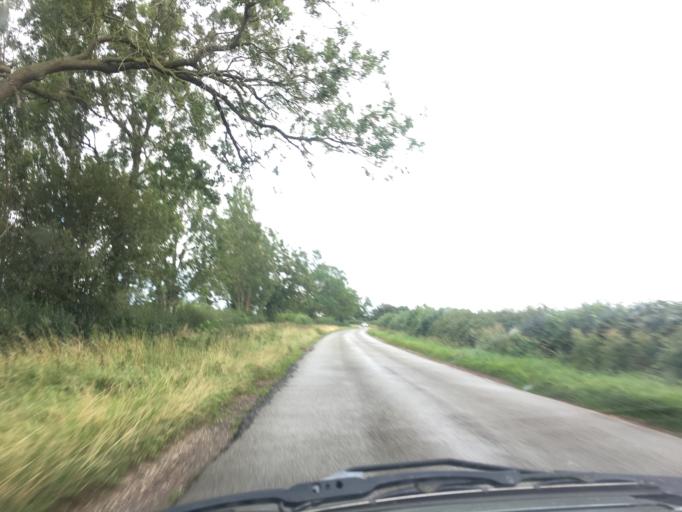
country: GB
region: England
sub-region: Leicestershire
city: Sapcote
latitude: 52.5212
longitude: -1.2784
